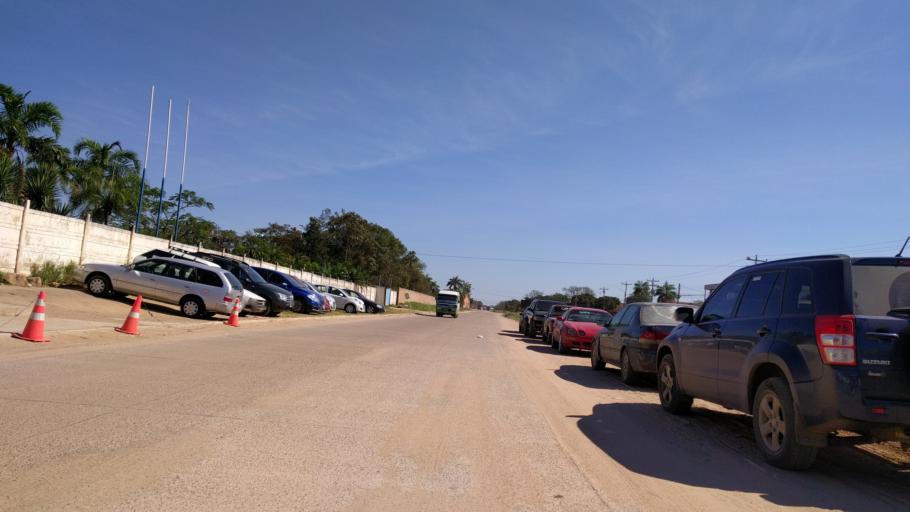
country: BO
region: Santa Cruz
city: Santa Cruz de la Sierra
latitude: -17.8436
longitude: -63.2307
